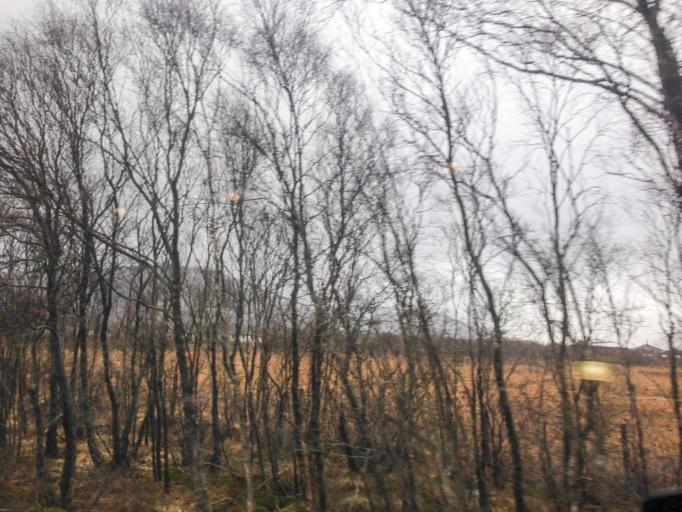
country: GB
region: Scotland
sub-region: Highland
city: Fort William
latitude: 56.8400
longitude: -5.0902
